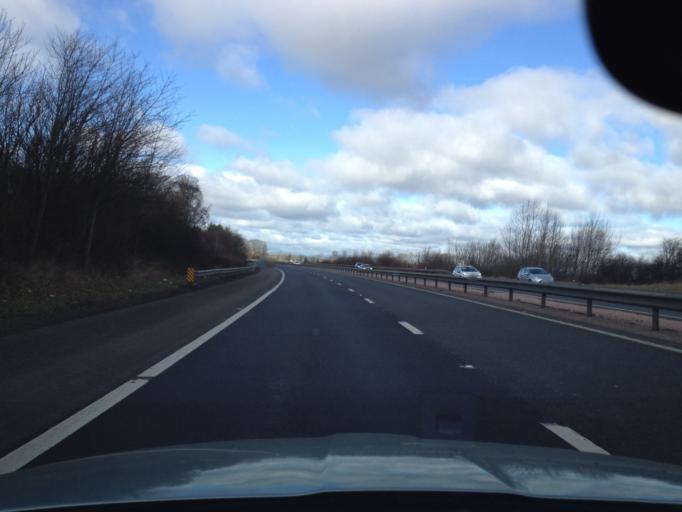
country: GB
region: Scotland
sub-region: Edinburgh
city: Ratho
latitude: 55.9272
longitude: -3.3503
